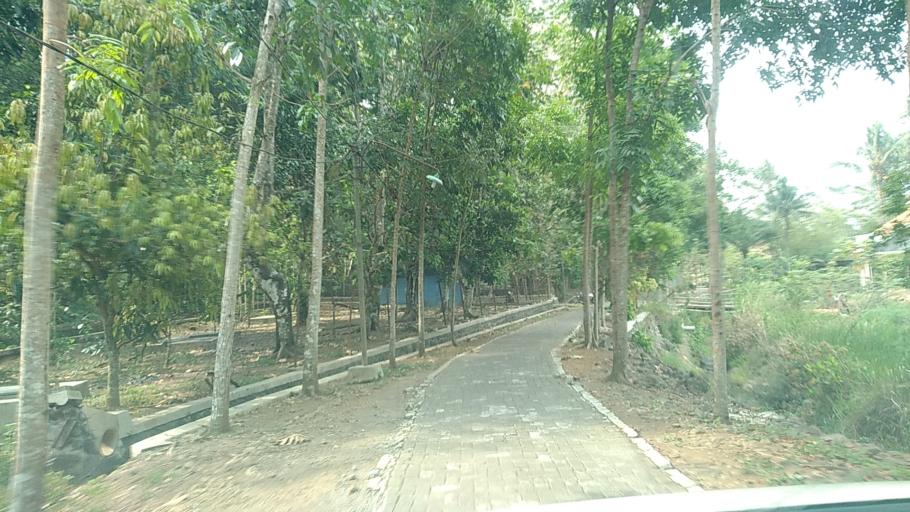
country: ID
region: Central Java
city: Ungaran
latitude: -7.1090
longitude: 110.3850
